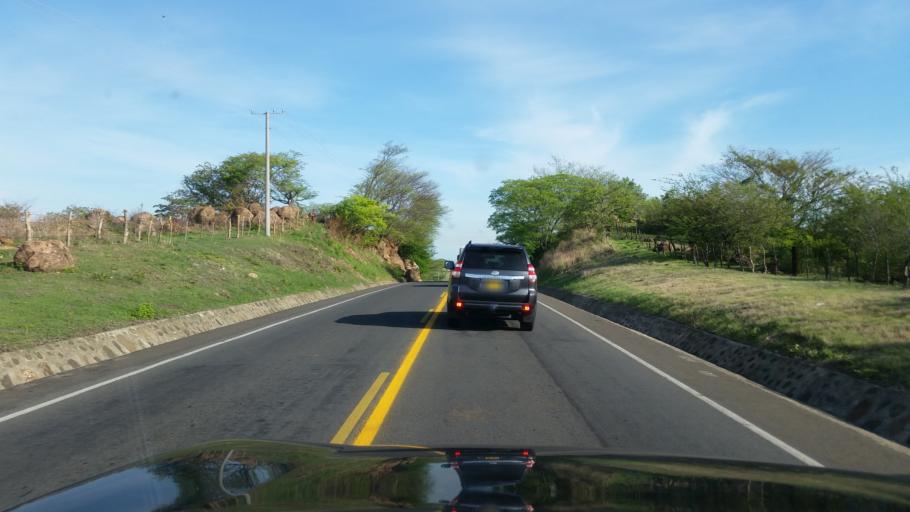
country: NI
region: Leon
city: La Paz Centro
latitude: 12.2270
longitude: -86.6992
